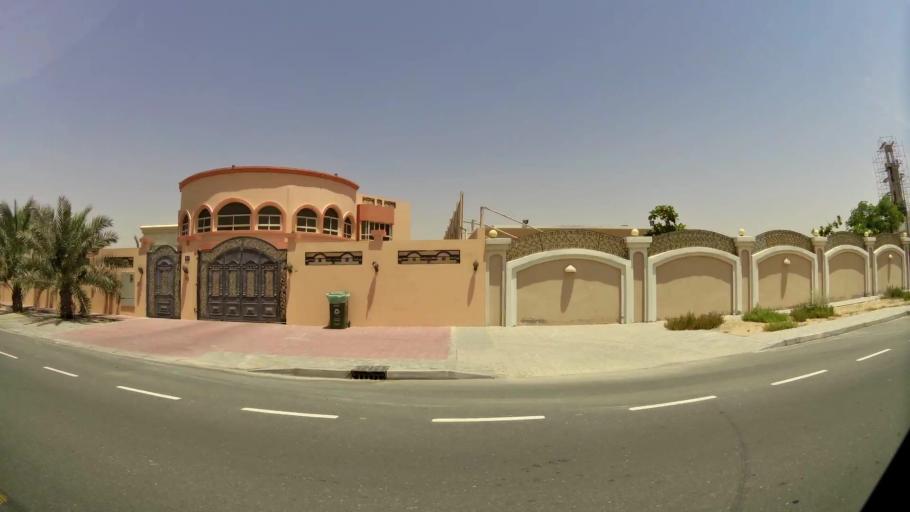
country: AE
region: Dubai
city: Dubai
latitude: 25.0873
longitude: 55.2003
